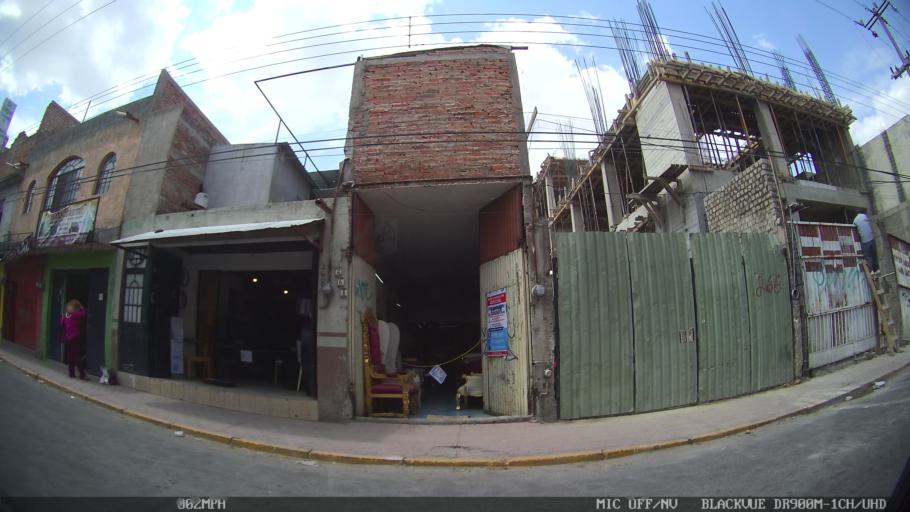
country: MX
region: Jalisco
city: Tonala
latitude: 20.6256
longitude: -103.2475
